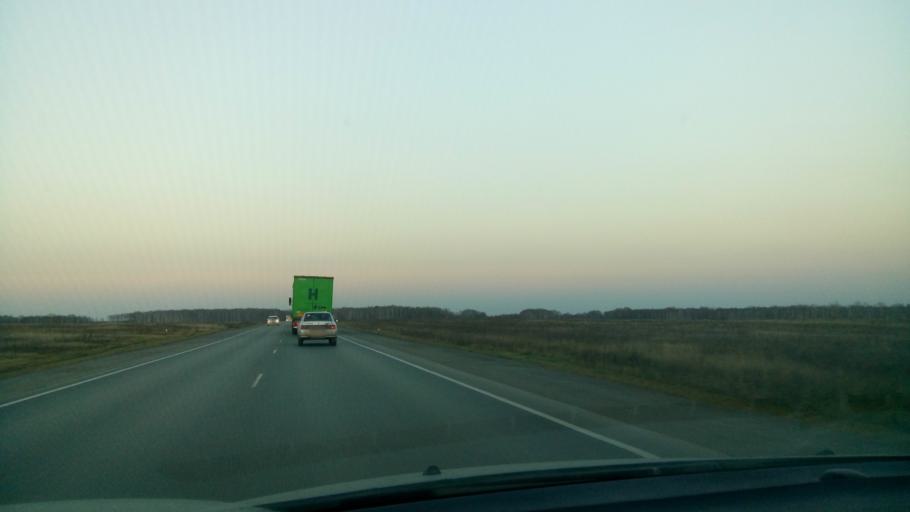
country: RU
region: Sverdlovsk
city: Pyshma
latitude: 56.9216
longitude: 63.1404
